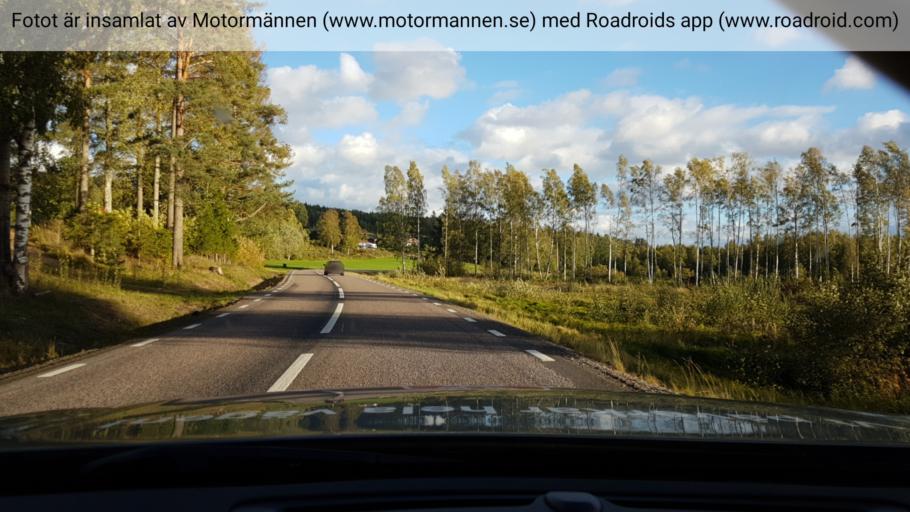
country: SE
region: Vaermland
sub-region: Karlstads Kommun
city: Molkom
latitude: 59.6768
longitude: 13.6829
